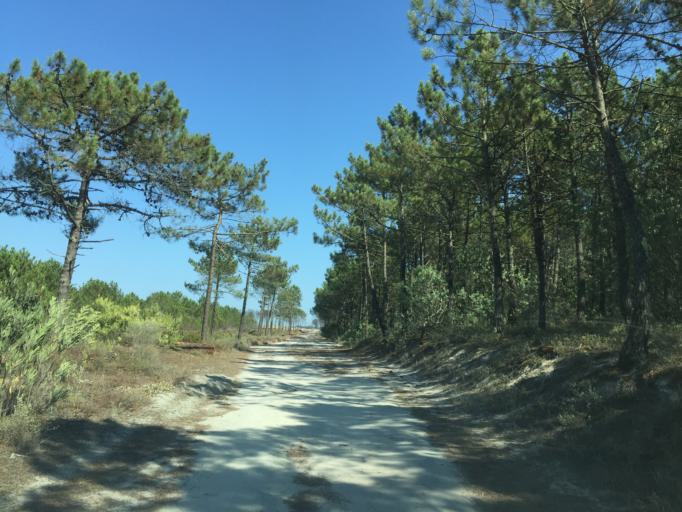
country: PT
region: Coimbra
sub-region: Figueira da Foz
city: Tavarede
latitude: 40.2583
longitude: -8.8421
